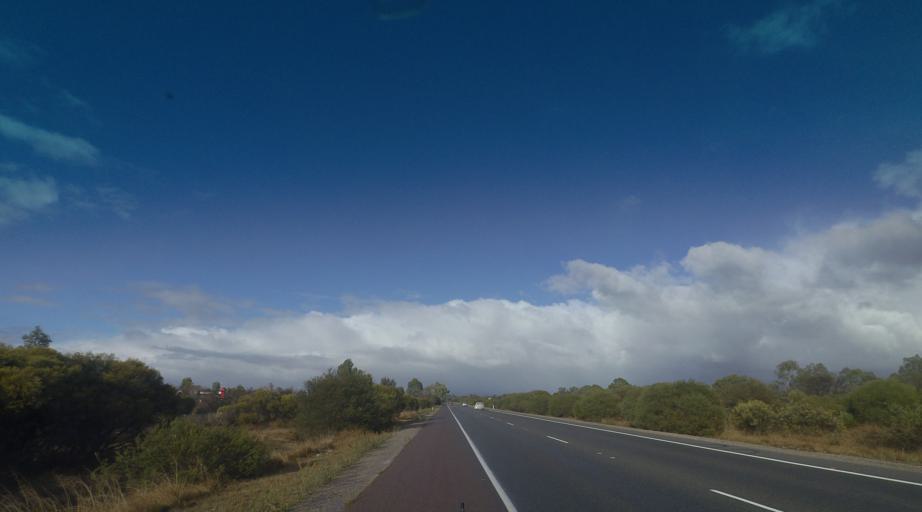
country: AU
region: Western Australia
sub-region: Gosnells
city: Southern River
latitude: -32.1360
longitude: 115.9596
